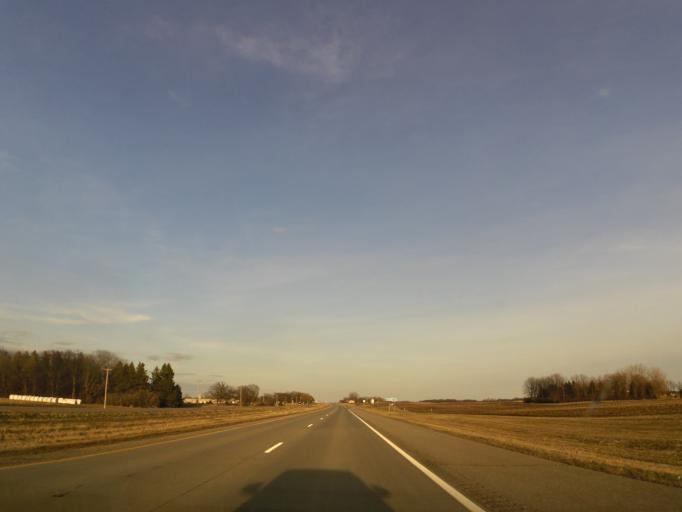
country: US
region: Minnesota
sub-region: McLeod County
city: Glencoe
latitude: 44.7679
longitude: -94.0546
